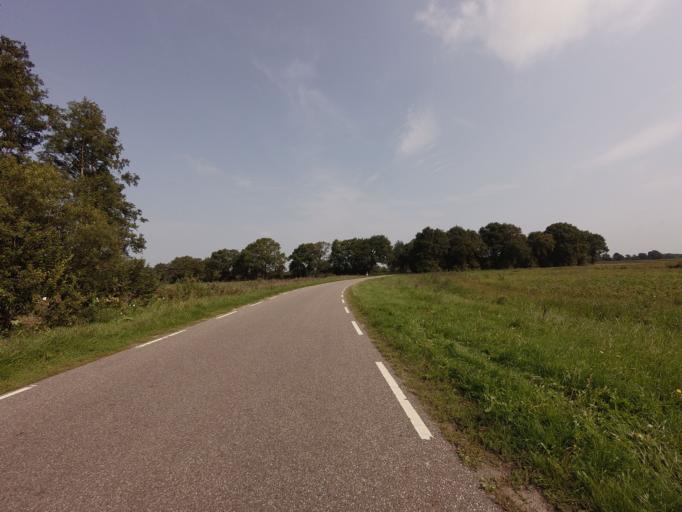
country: NL
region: Drenthe
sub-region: Gemeente Assen
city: Assen
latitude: 52.9580
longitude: 6.6062
